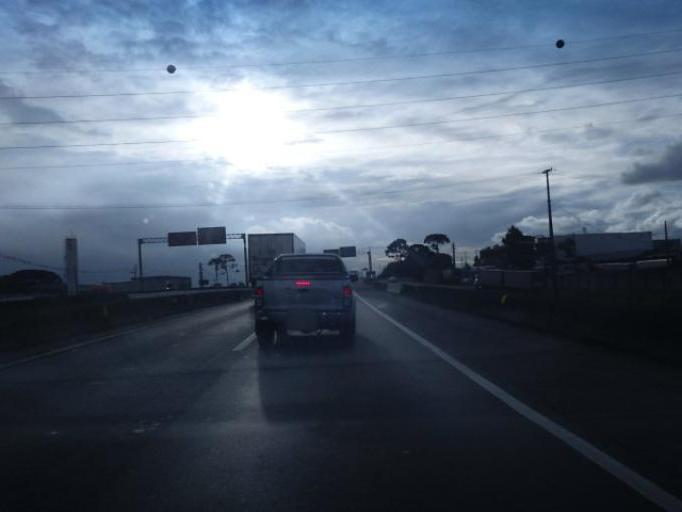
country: BR
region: Parana
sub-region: Sao Jose Dos Pinhais
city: Sao Jose dos Pinhais
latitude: -25.5675
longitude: -49.1731
